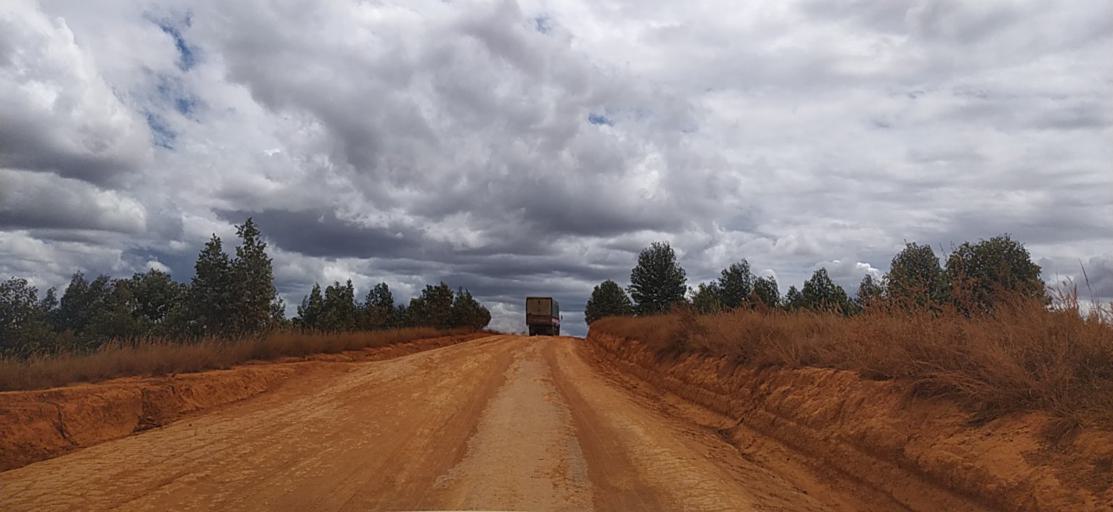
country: MG
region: Alaotra Mangoro
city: Ambatondrazaka
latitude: -18.0561
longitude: 48.2542
